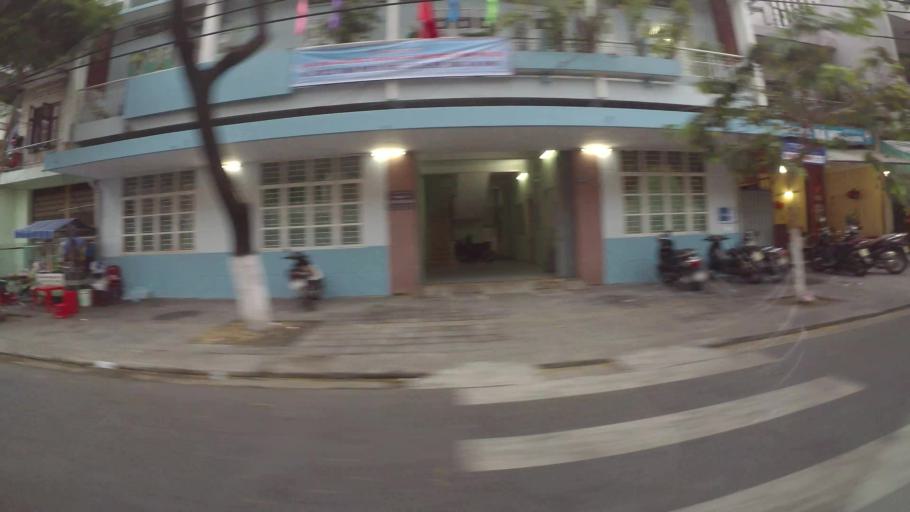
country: VN
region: Da Nang
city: Da Nang
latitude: 16.0639
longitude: 108.2216
